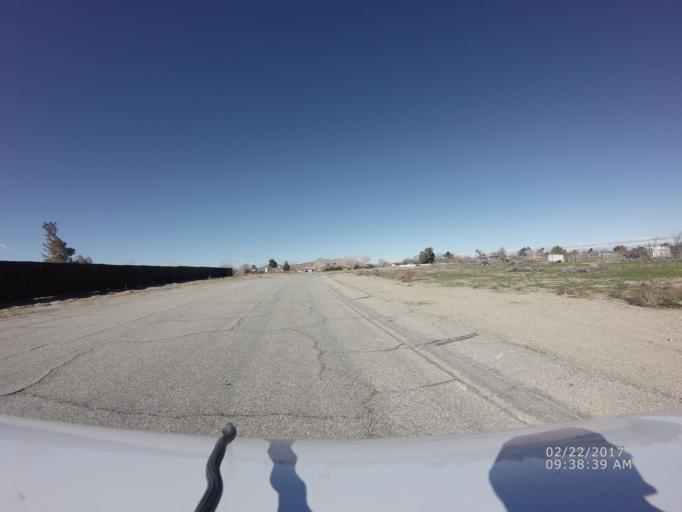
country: US
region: California
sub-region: Los Angeles County
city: Lake Los Angeles
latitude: 34.6275
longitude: -117.8439
